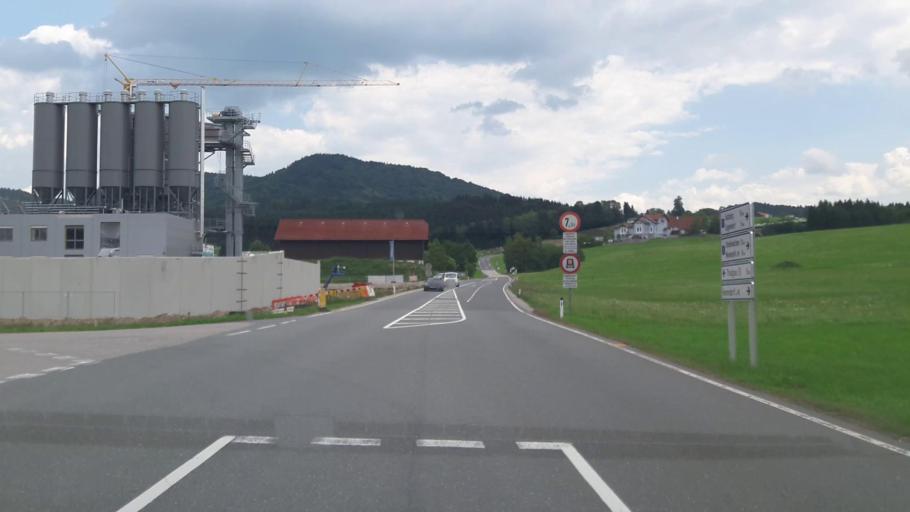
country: AT
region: Salzburg
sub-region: Politischer Bezirk Salzburg-Umgebung
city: Henndorf am Wallersee
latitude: 47.8881
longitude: 13.1869
